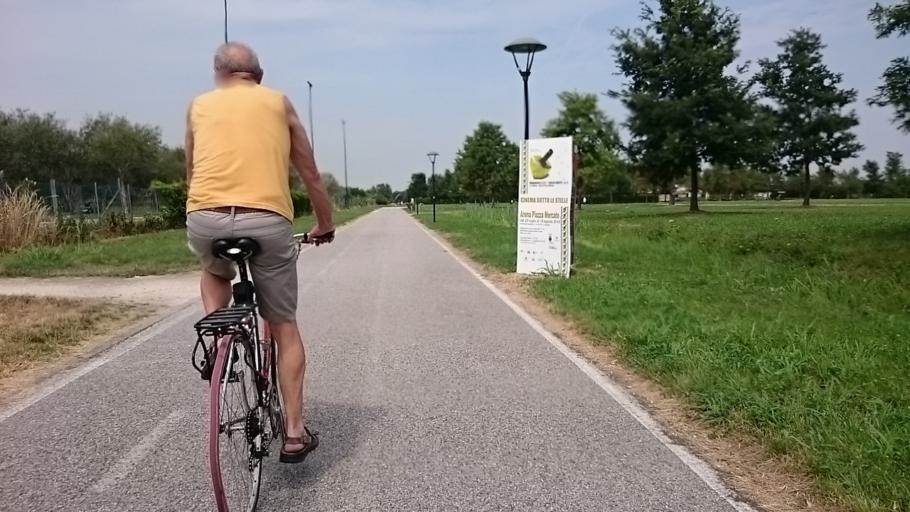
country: IT
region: Veneto
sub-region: Provincia di Venezia
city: Campalto
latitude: 45.4681
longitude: 12.2802
